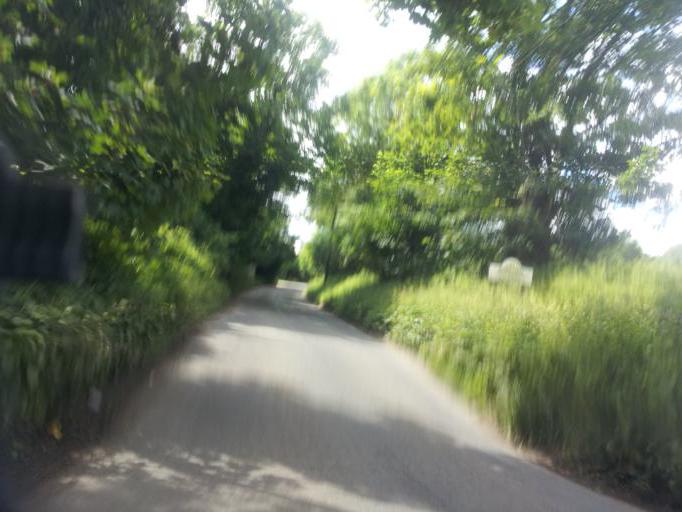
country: GB
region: England
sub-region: Kent
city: West Malling
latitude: 51.3216
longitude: 0.4113
